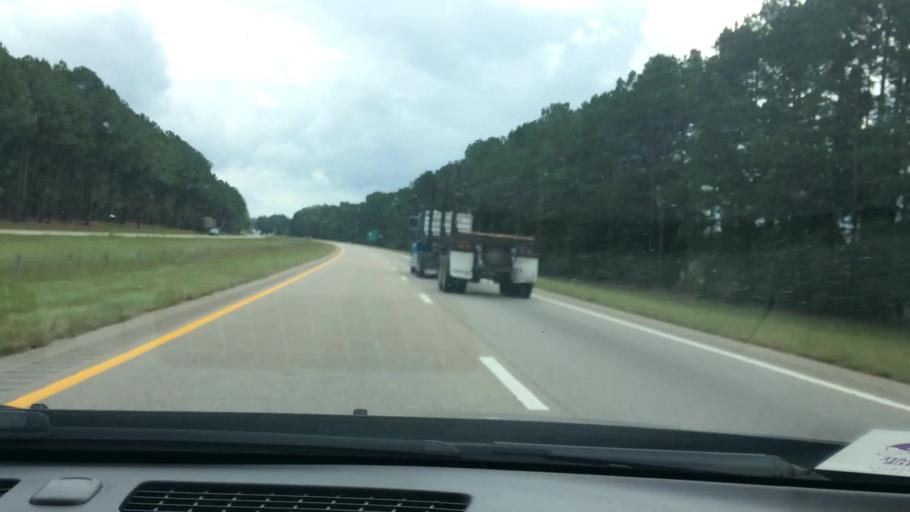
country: US
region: North Carolina
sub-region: Wake County
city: Zebulon
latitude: 35.8250
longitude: -78.2832
